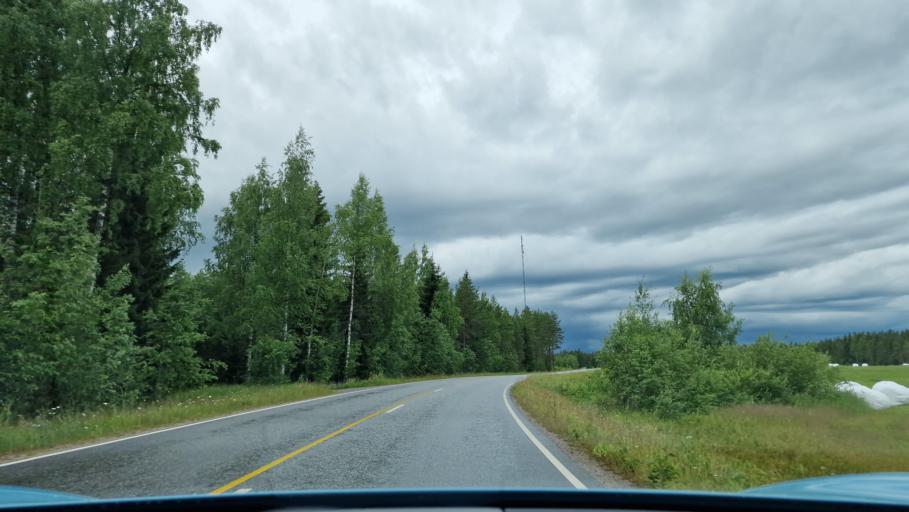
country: FI
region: Southern Ostrobothnia
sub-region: Jaerviseutu
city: Soini
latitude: 62.6817
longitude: 24.4777
